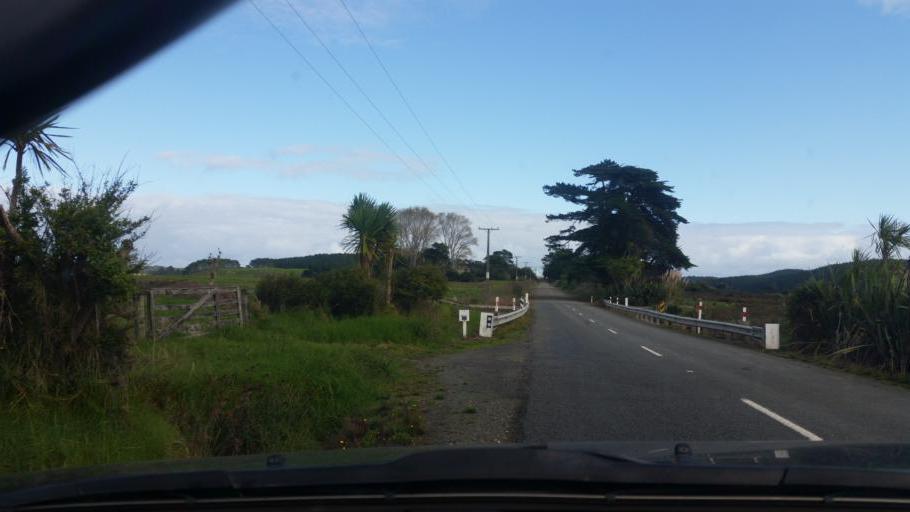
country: NZ
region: Northland
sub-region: Kaipara District
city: Dargaville
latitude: -35.9063
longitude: 173.8088
